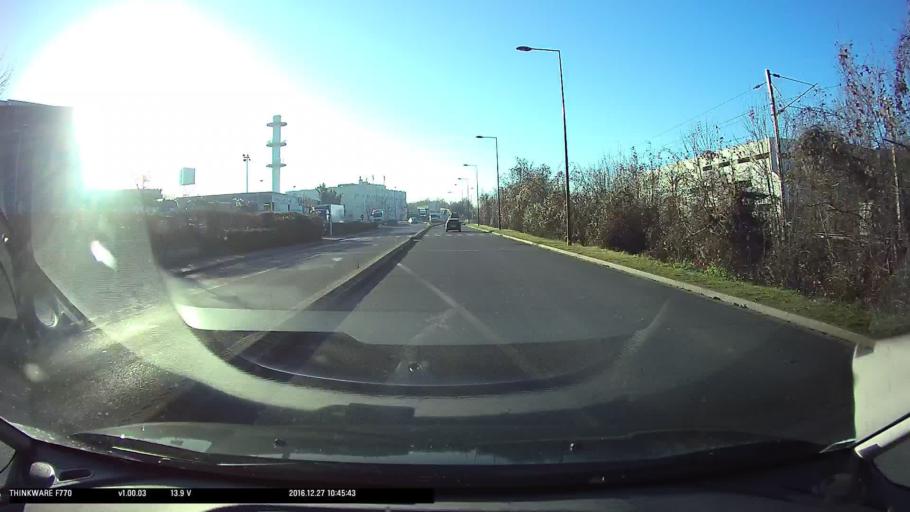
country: FR
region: Ile-de-France
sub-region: Departement du Val-d'Oise
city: Eragny
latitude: 49.0319
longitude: 2.1015
